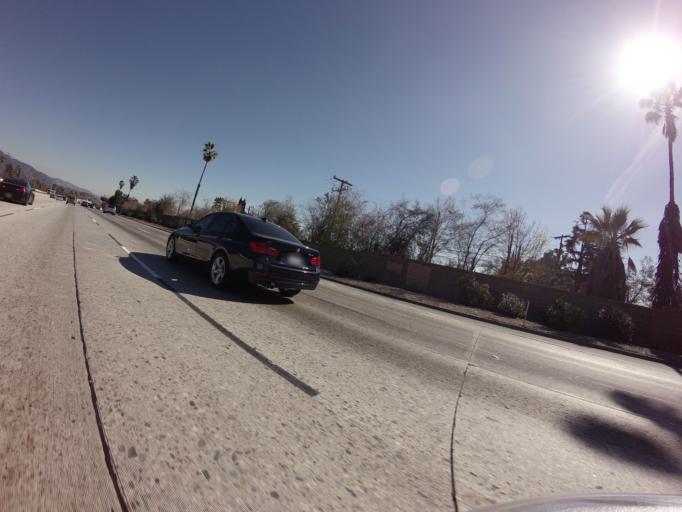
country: US
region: California
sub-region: Los Angeles County
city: Bradbury
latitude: 34.1340
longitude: -117.9568
